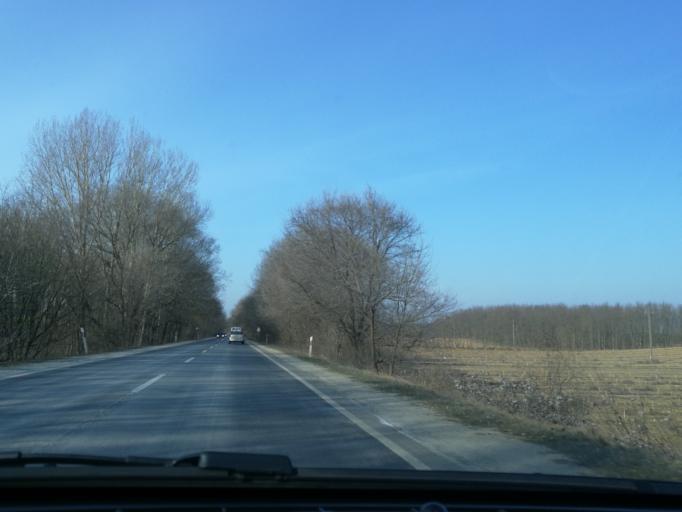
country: HU
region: Szabolcs-Szatmar-Bereg
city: Apagy
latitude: 47.9556
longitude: 21.9109
